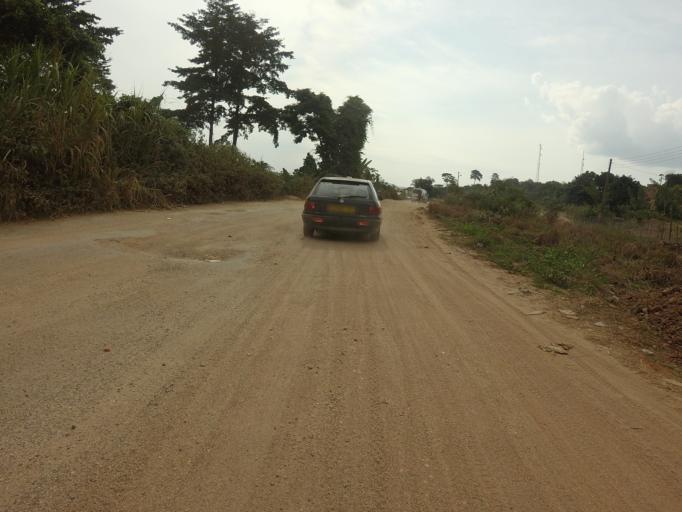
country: GH
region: Volta
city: Ho
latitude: 6.6832
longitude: 0.3354
